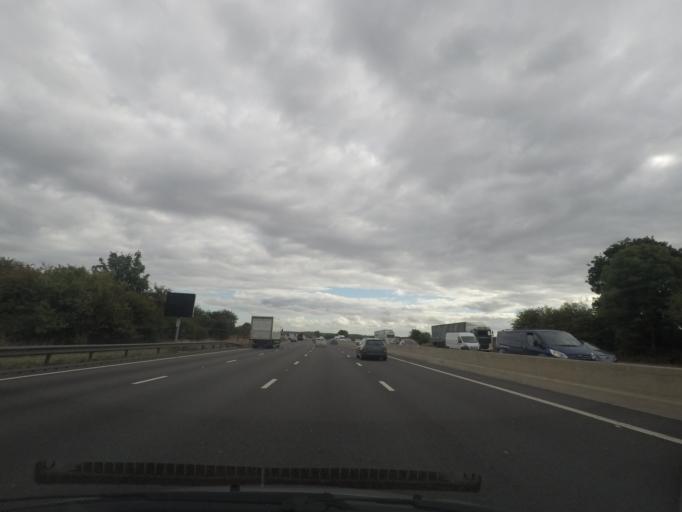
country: GB
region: England
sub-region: Rotherham
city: Wales
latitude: 53.3385
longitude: -1.2895
